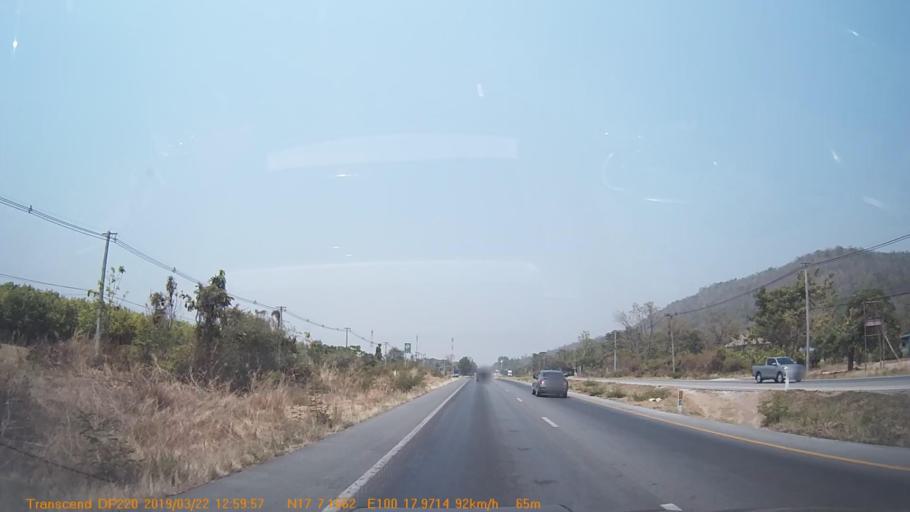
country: TH
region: Phitsanulok
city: Phrom Phiram
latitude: 17.1198
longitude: 100.2994
